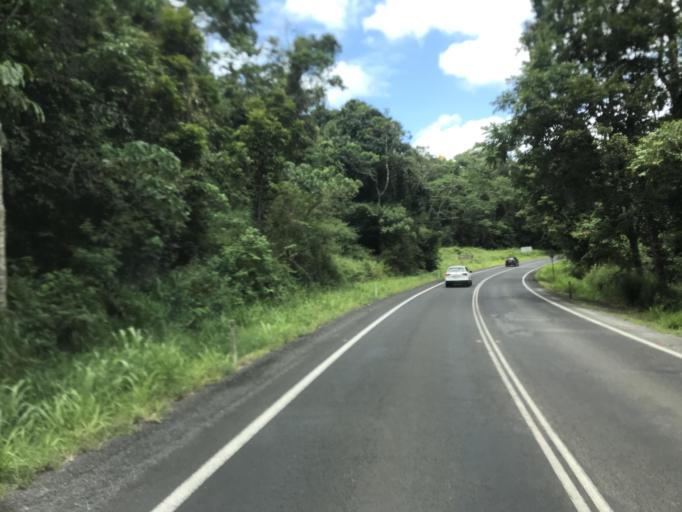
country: AU
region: Queensland
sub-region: Tablelands
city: Ravenshoe
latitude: -17.6043
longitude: 145.7614
